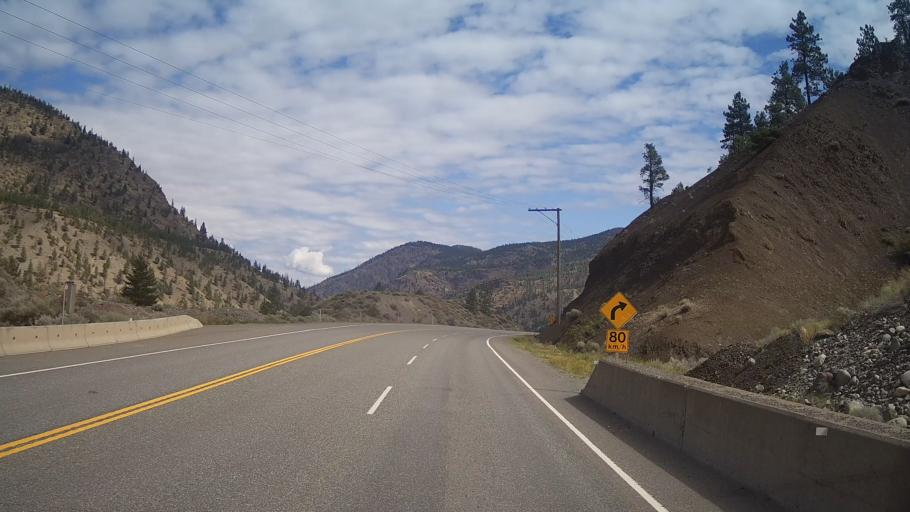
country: CA
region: British Columbia
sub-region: Thompson-Nicola Regional District
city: Ashcroft
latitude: 50.2855
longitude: -121.4017
